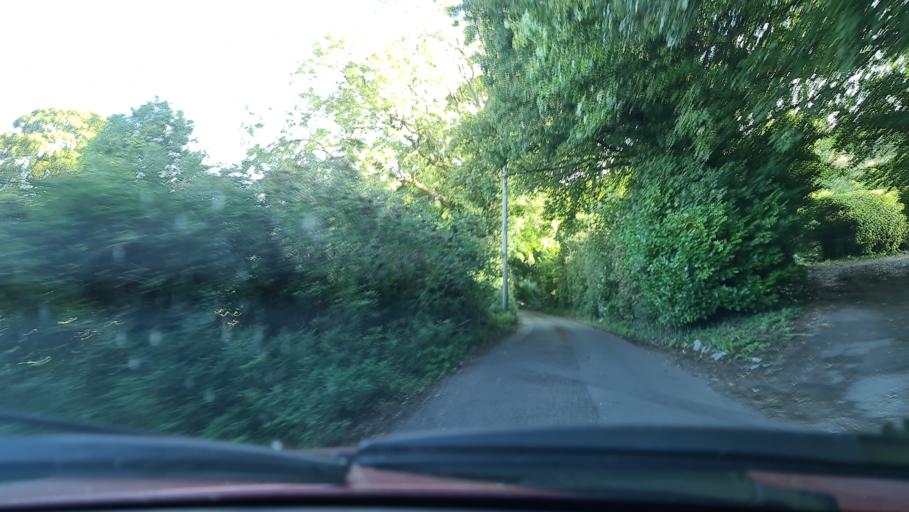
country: GB
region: England
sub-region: Buckinghamshire
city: Princes Risborough
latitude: 51.7061
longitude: -0.8195
